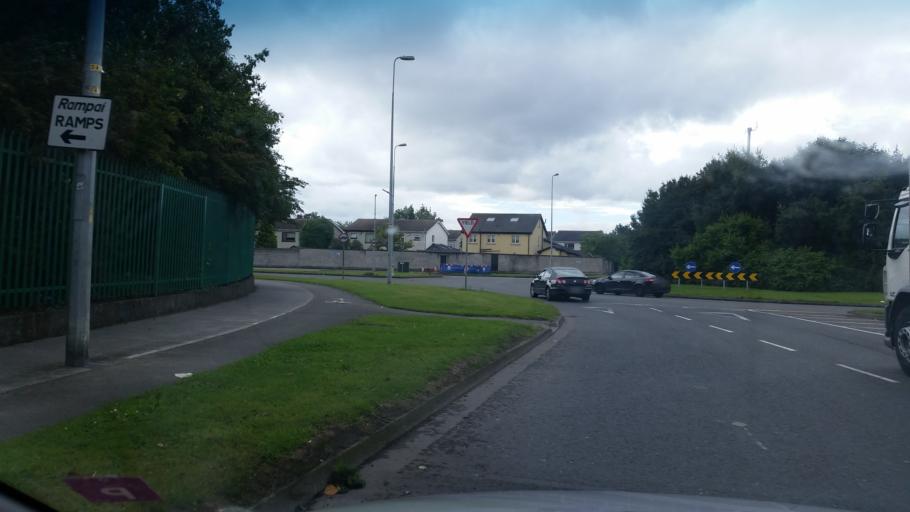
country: IE
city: Darndale
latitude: 53.3979
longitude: -6.1861
